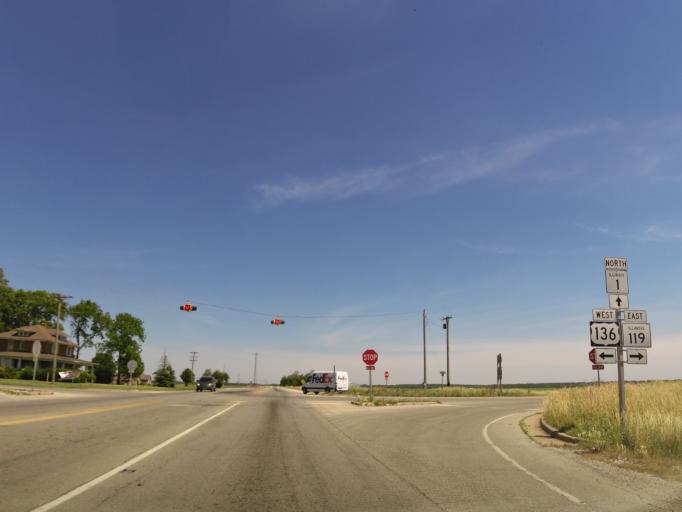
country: US
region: Illinois
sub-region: Vermilion County
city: Rossville
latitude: 40.2991
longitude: -87.6580
